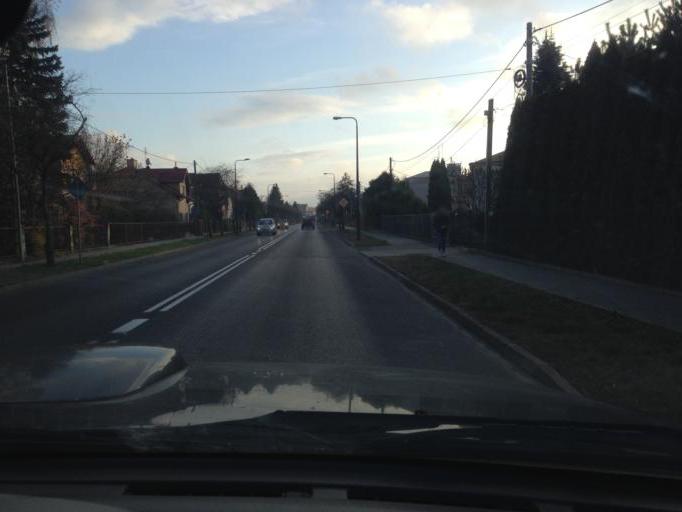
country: PL
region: Subcarpathian Voivodeship
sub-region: Powiat jasielski
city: Jaslo
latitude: 49.7572
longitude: 21.4720
